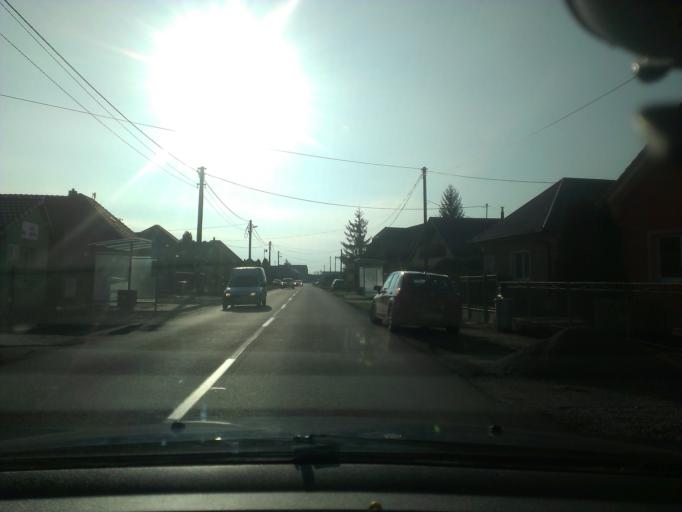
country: SK
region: Nitriansky
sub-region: Okres Nitra
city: Nitra
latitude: 48.3740
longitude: 18.0243
